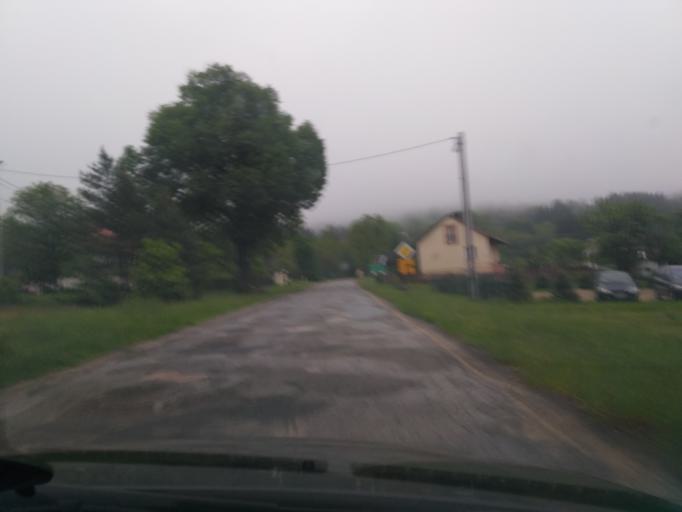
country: PL
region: Subcarpathian Voivodeship
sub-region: Powiat debicki
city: Debica
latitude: 49.9734
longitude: 21.3819
